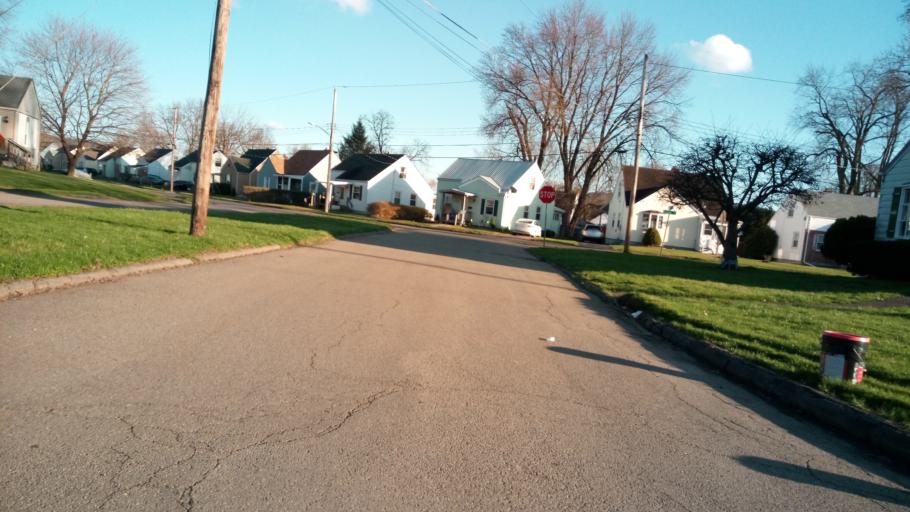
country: US
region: New York
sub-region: Chemung County
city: Elmira
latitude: 42.0803
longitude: -76.7865
